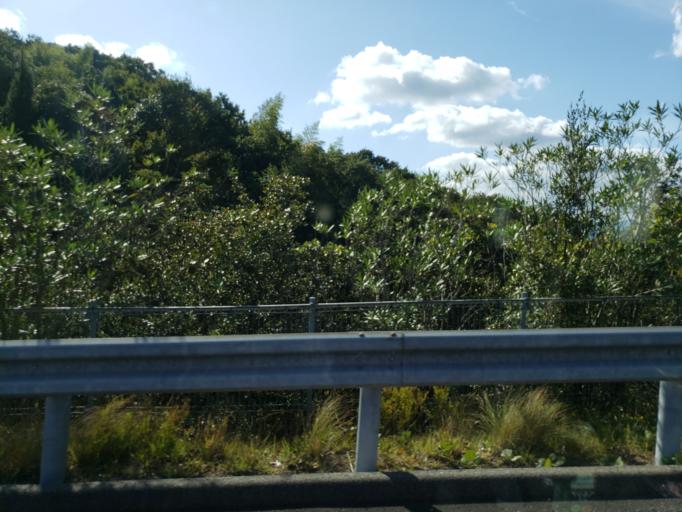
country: JP
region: Tokushima
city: Ishii
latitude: 34.1428
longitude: 134.4364
